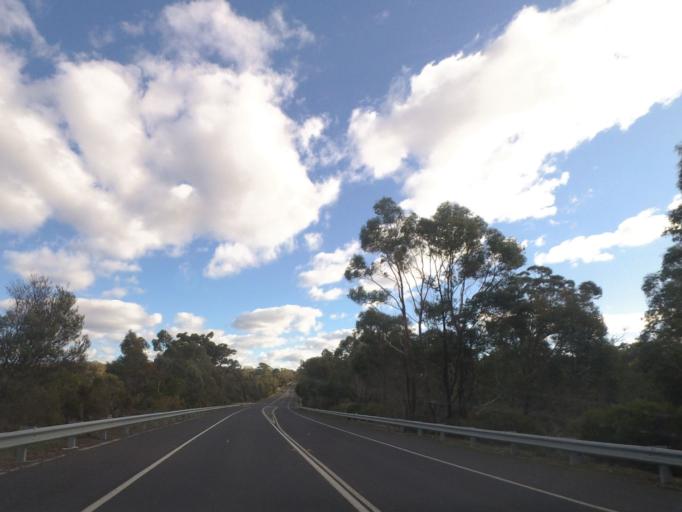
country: AU
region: Victoria
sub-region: Mount Alexander
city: Castlemaine
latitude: -37.1026
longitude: 144.3183
